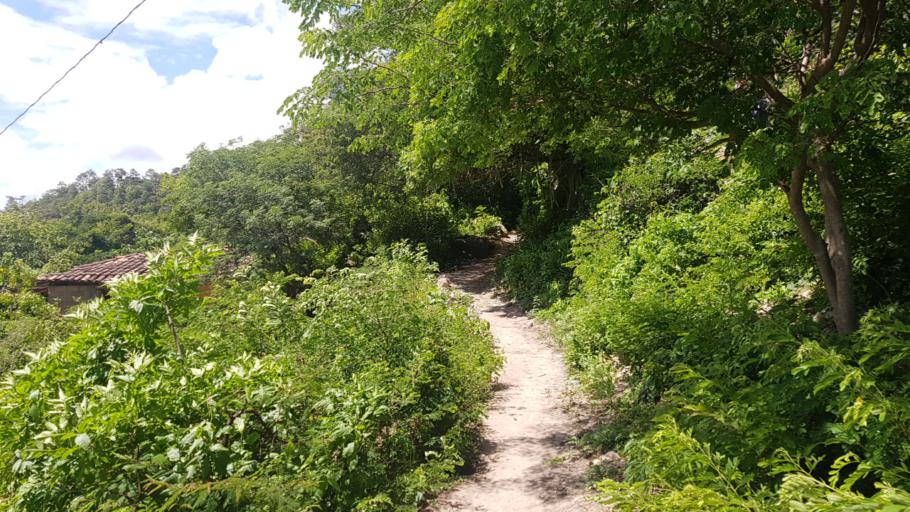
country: NI
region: Madriz
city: Somoto
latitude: 13.6045
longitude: -86.6143
